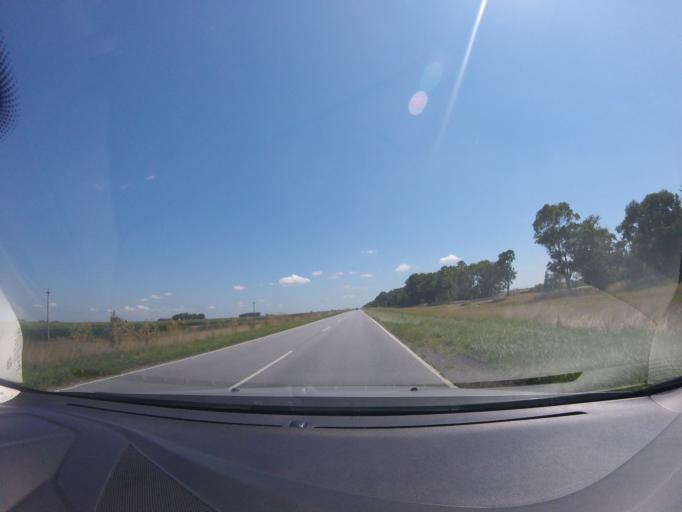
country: AR
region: Buenos Aires
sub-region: Partido de Tandil
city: Tandil
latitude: -37.0836
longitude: -58.9993
